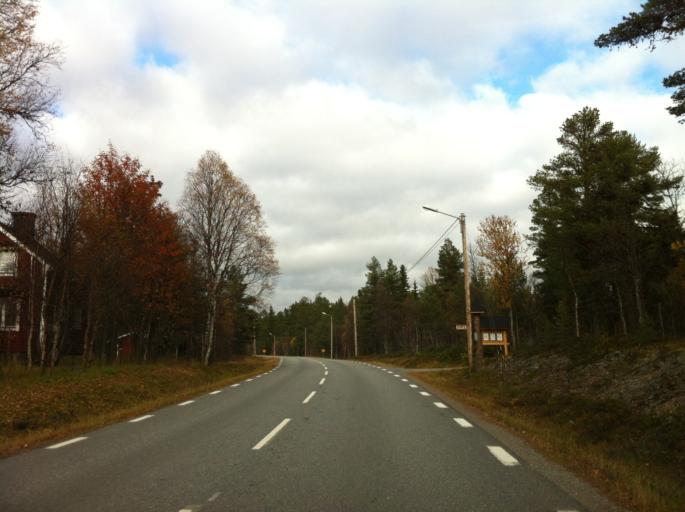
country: NO
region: Hedmark
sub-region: Engerdal
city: Engerdal
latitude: 62.0623
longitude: 12.3178
